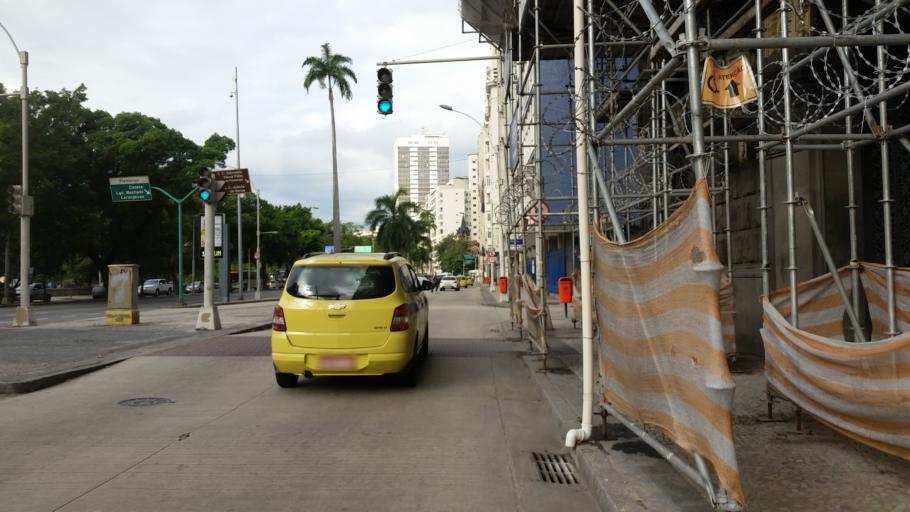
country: BR
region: Rio de Janeiro
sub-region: Rio De Janeiro
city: Rio de Janeiro
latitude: -22.9275
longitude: -43.1737
